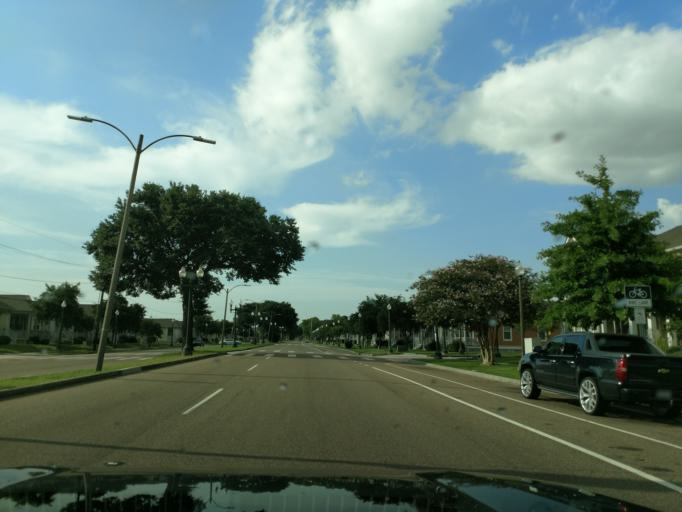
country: US
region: Louisiana
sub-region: Jefferson Parish
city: Gretna
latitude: 29.9310
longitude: -90.0417
